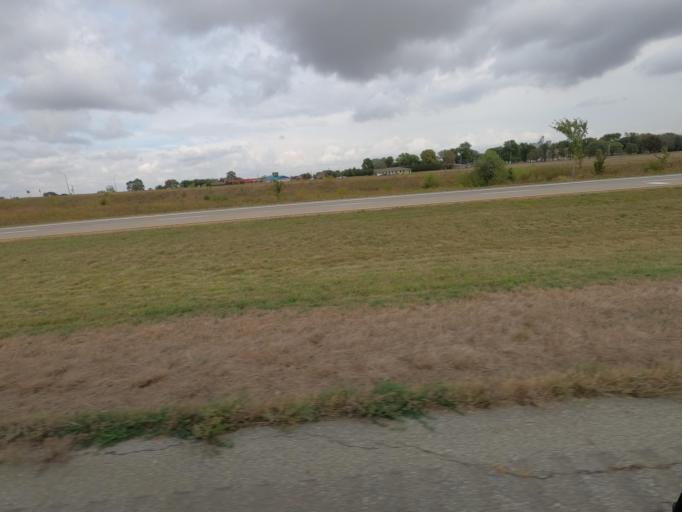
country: US
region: Iowa
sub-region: Jasper County
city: Prairie City
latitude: 41.5934
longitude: -93.2487
